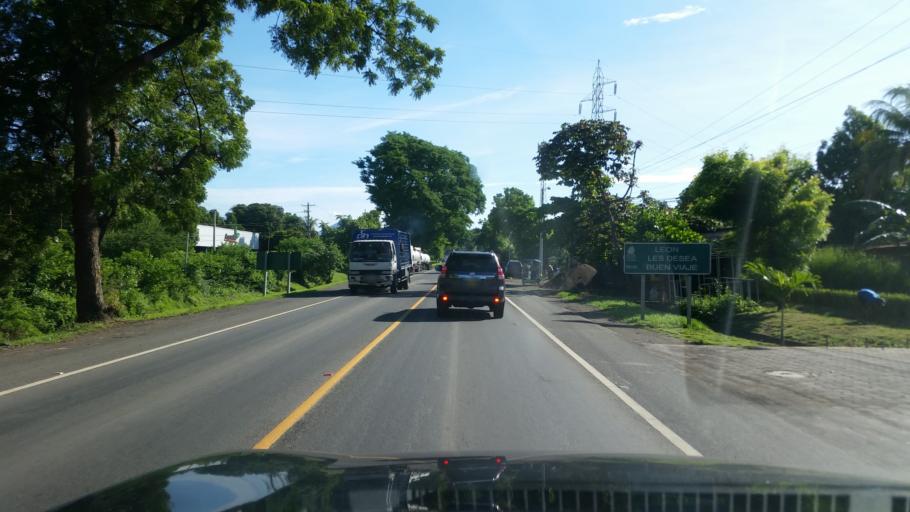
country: NI
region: Leon
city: Leon
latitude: 12.4625
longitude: -86.8668
